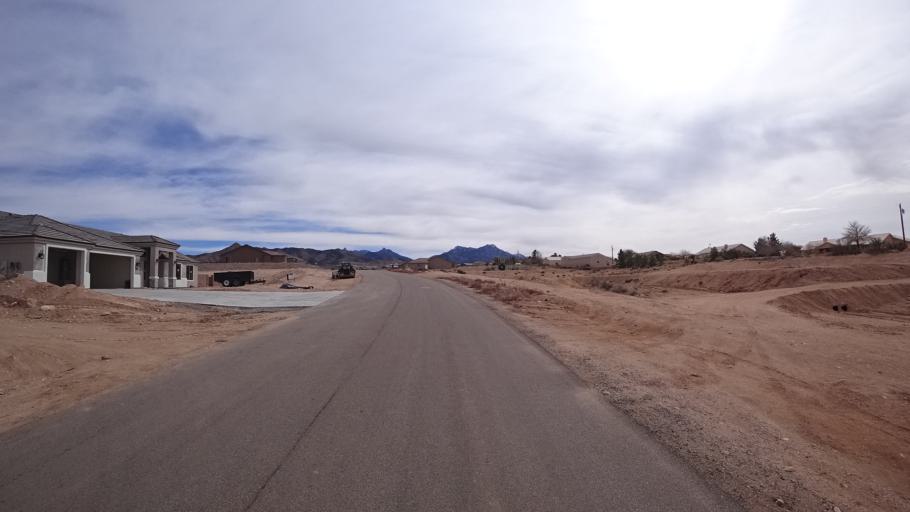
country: US
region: Arizona
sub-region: Mohave County
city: Kingman
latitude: 35.1872
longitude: -113.9815
